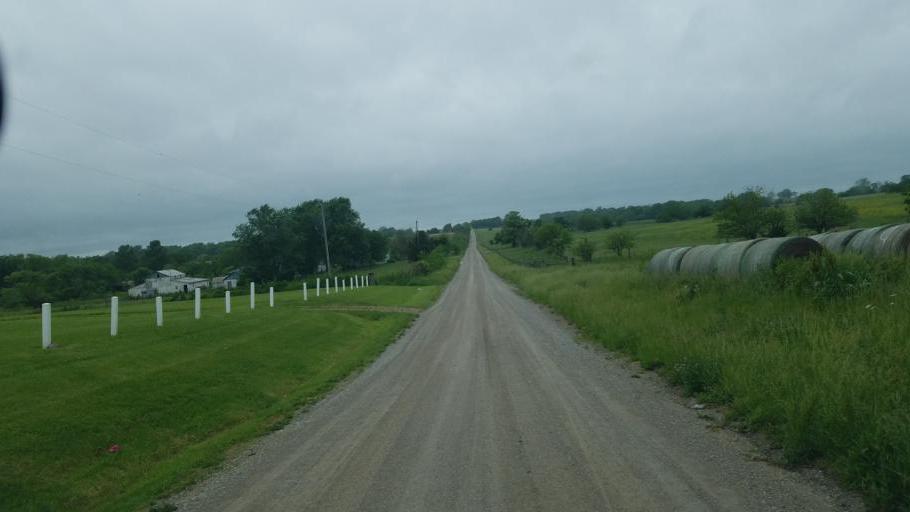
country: US
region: Missouri
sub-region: Carroll County
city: Carrollton
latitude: 39.4851
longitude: -93.4760
